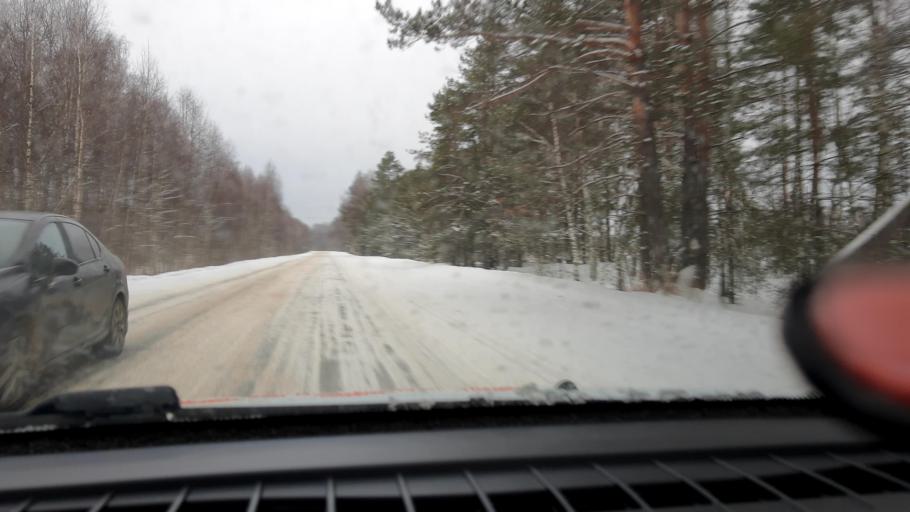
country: RU
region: Nizjnij Novgorod
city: Pamyat' Parizhskoy Kommuny
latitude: 56.2618
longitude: 44.4461
